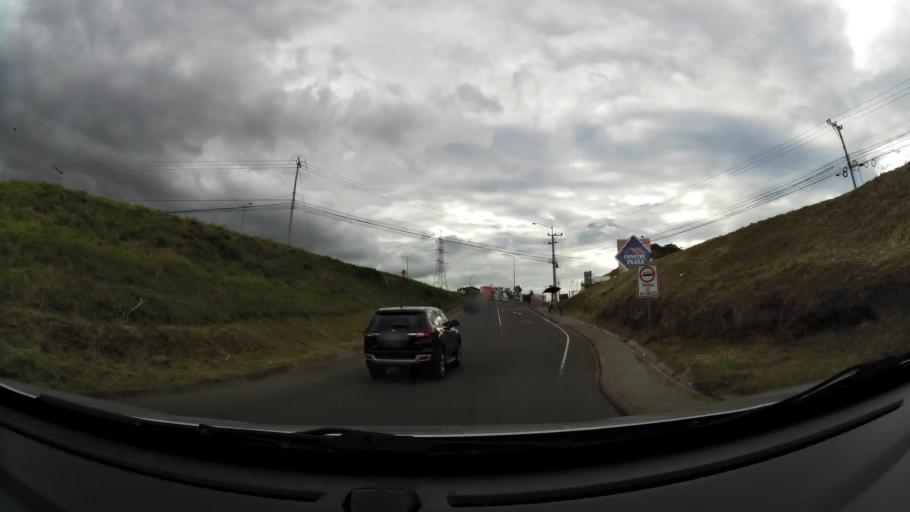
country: CR
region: San Jose
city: Santa Ana
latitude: 9.9475
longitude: -84.1622
